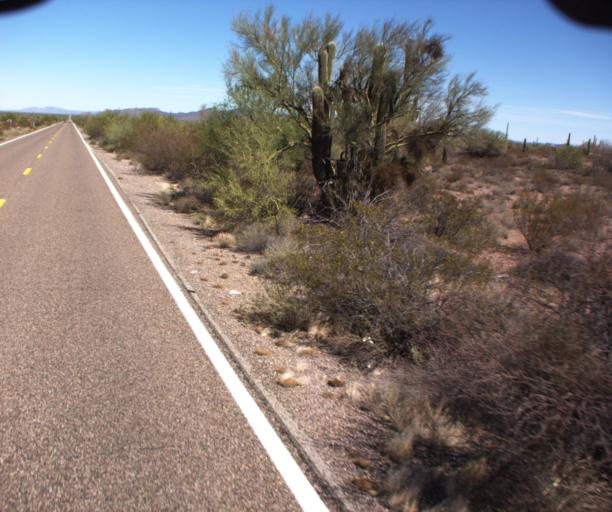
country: MX
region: Sonora
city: Sonoyta
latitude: 32.1129
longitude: -112.7697
